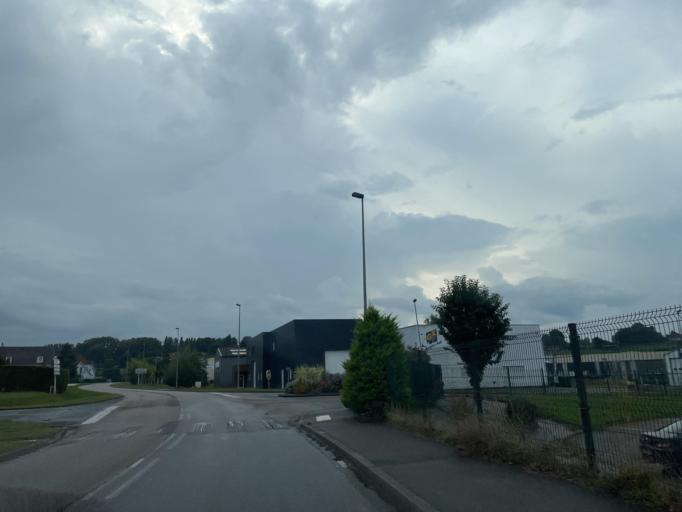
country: FR
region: Haute-Normandie
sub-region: Departement de la Seine-Maritime
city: Neufchatel-en-Bray
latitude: 49.7257
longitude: 1.4371
